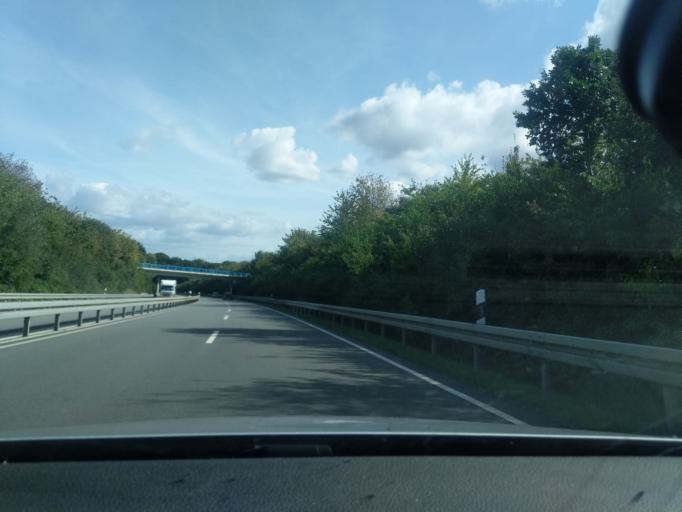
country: DE
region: Lower Saxony
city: Ostercappeln
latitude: 52.3396
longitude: 8.2366
